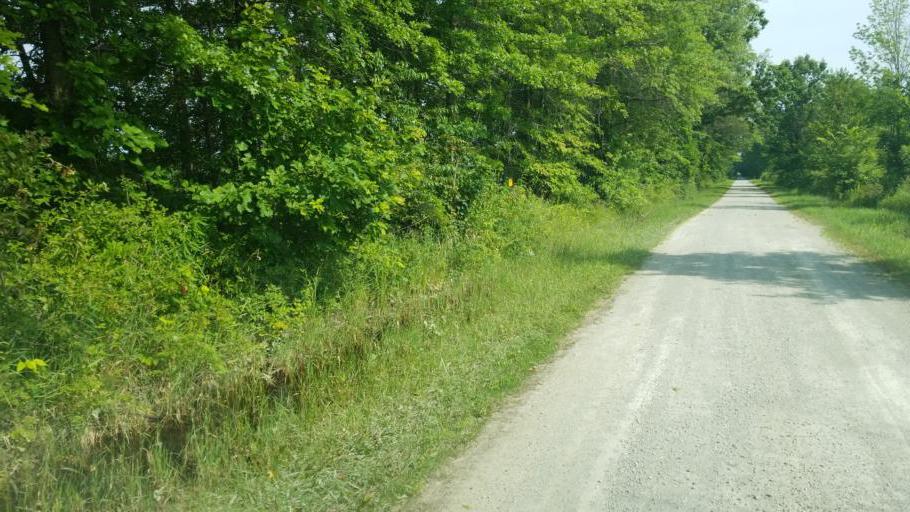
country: US
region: Ohio
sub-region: Wyandot County
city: Upper Sandusky
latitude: 40.7072
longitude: -83.3430
